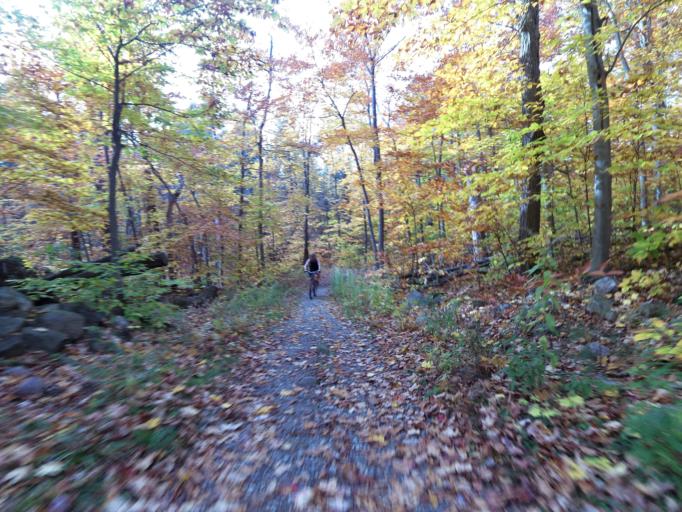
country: CA
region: Quebec
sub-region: Outaouais
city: Gatineau
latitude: 45.4813
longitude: -75.8415
